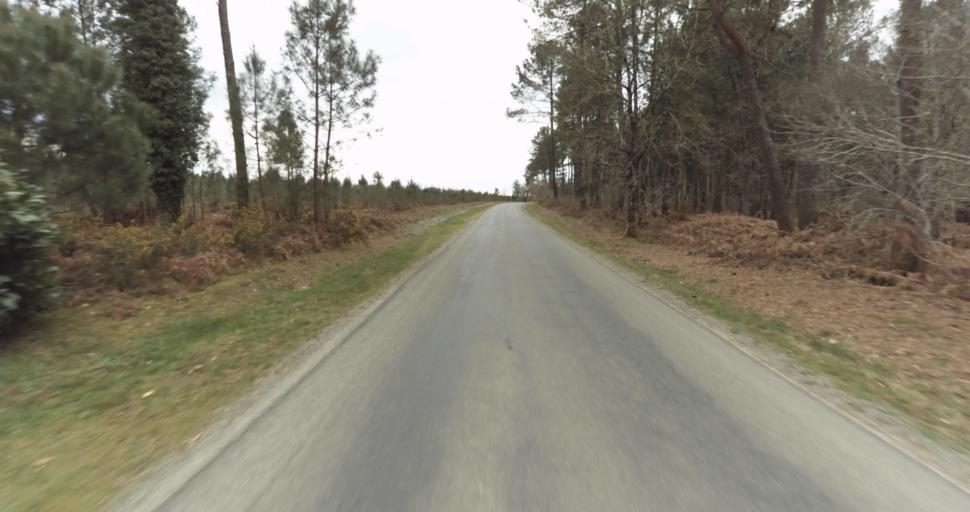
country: FR
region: Aquitaine
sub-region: Departement des Landes
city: Sarbazan
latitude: 44.0102
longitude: -0.3273
